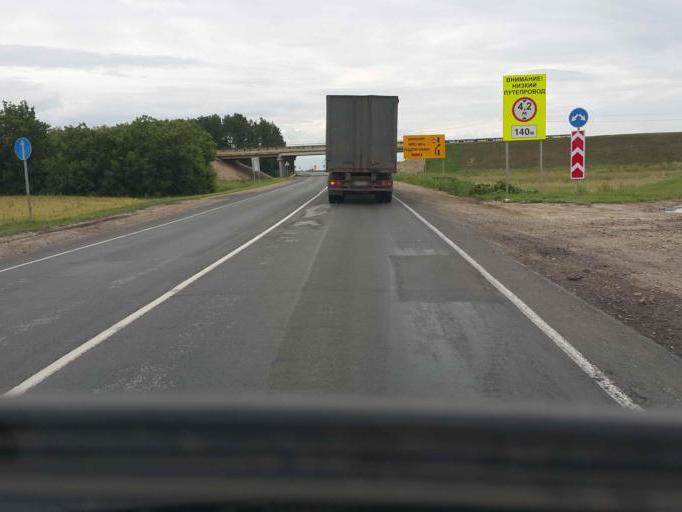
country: RU
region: Tambov
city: Zavoronezhskoye
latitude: 52.9110
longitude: 40.6322
